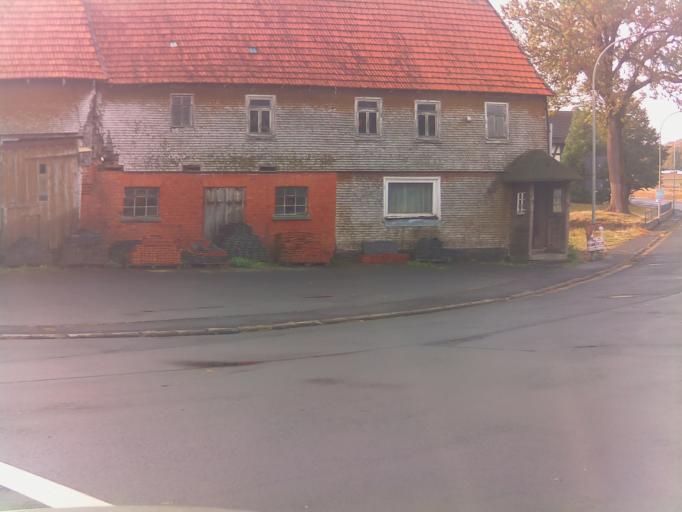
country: DE
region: Hesse
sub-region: Regierungsbezirk Giessen
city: Freiensteinau
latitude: 50.4830
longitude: 9.4020
